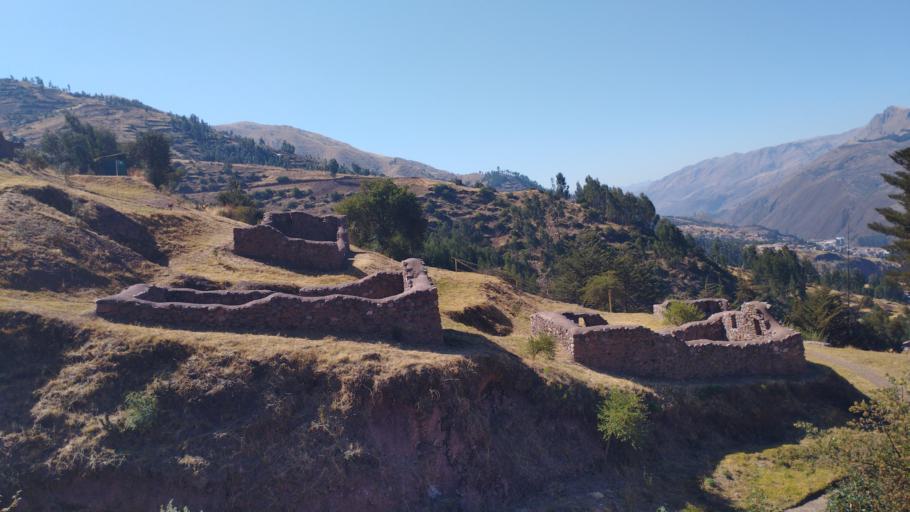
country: PE
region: Cusco
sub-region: Provincia de Cusco
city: Saylla
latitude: -13.5300
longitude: -71.8784
